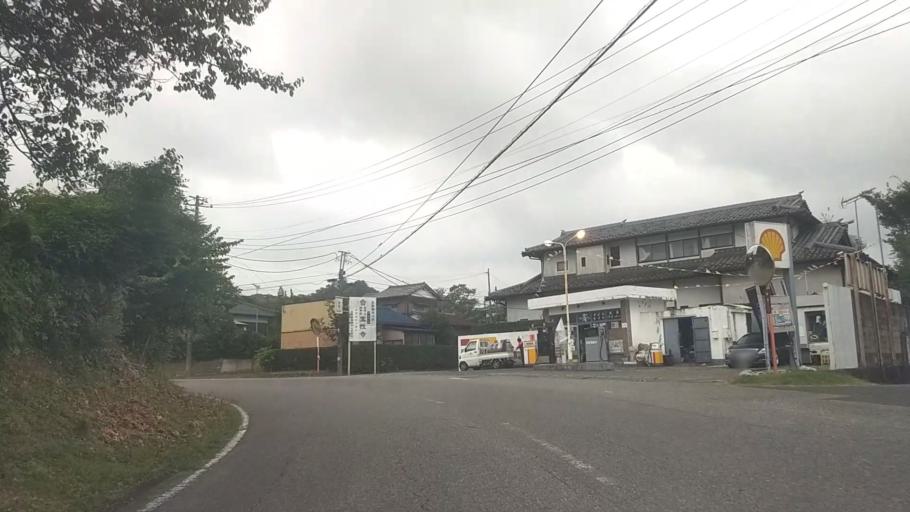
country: JP
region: Chiba
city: Kawaguchi
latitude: 35.2204
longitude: 140.0203
